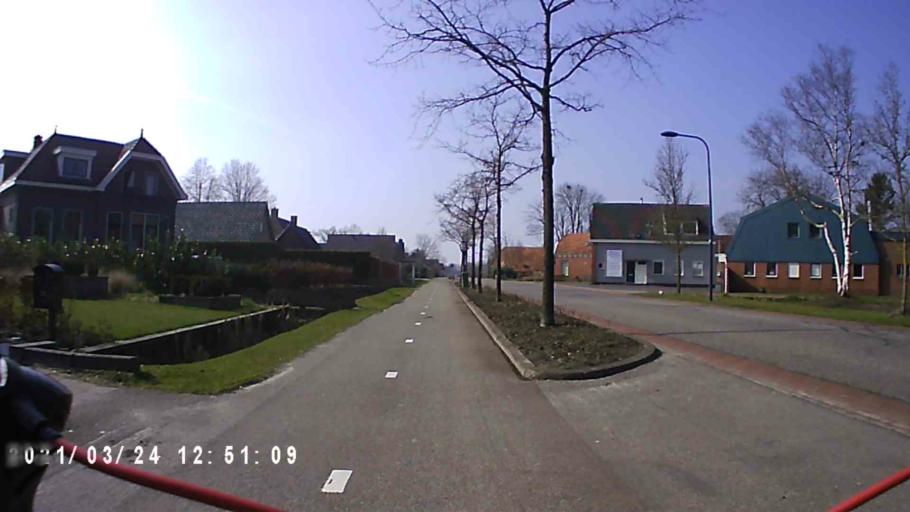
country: NL
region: Groningen
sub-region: Gemeente Leek
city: Leek
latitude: 53.1618
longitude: 6.3278
